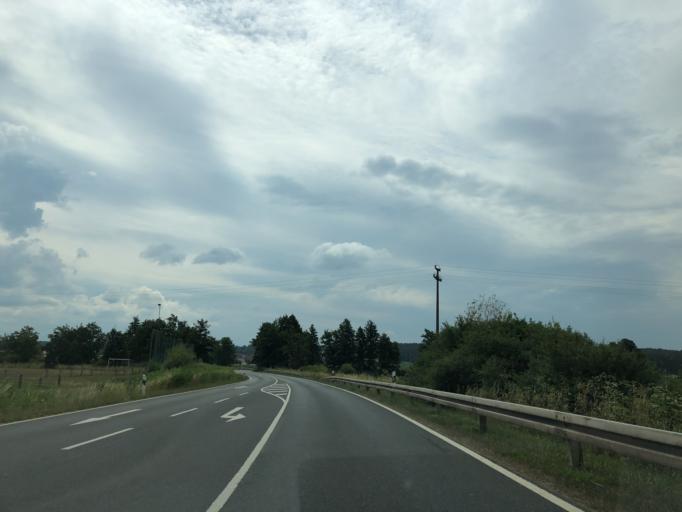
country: DE
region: Bavaria
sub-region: Regierungsbezirk Mittelfranken
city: Muhlhausen
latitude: 49.7516
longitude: 10.7690
